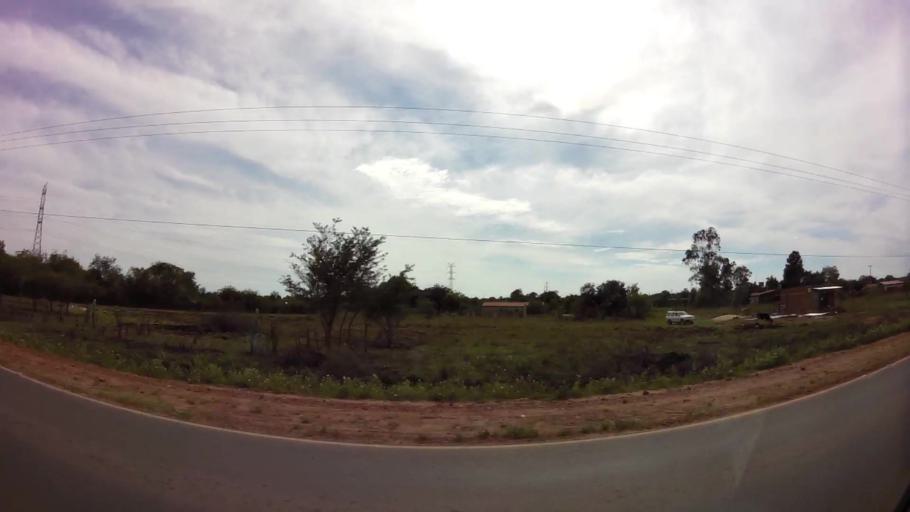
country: PY
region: Central
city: Limpio
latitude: -25.1287
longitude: -57.4822
